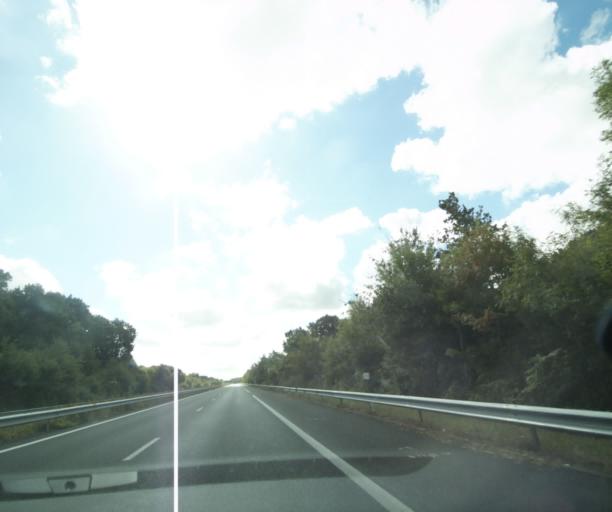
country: FR
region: Poitou-Charentes
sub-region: Departement de la Charente-Maritime
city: Cabariot
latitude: 45.9324
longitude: -0.8386
